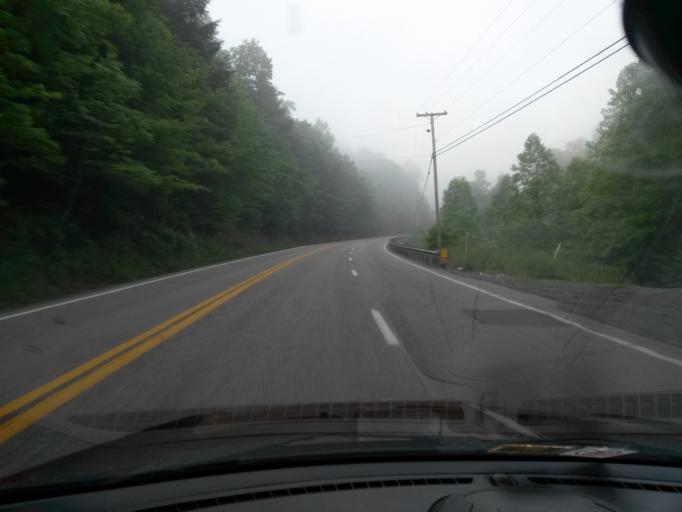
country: US
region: West Virginia
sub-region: McDowell County
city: Welch
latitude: 37.4936
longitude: -81.5388
